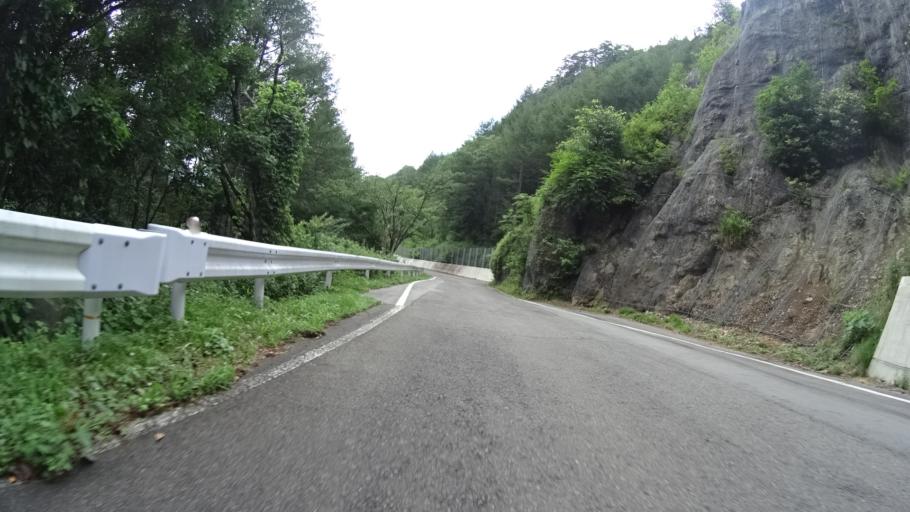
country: JP
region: Nagano
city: Saku
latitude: 36.0693
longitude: 138.6378
